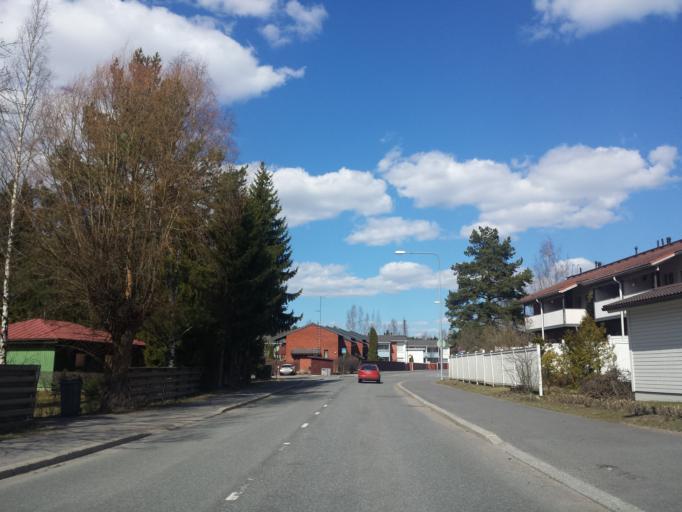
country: FI
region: Uusimaa
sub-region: Helsinki
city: Vantaa
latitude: 60.2978
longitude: 25.0171
